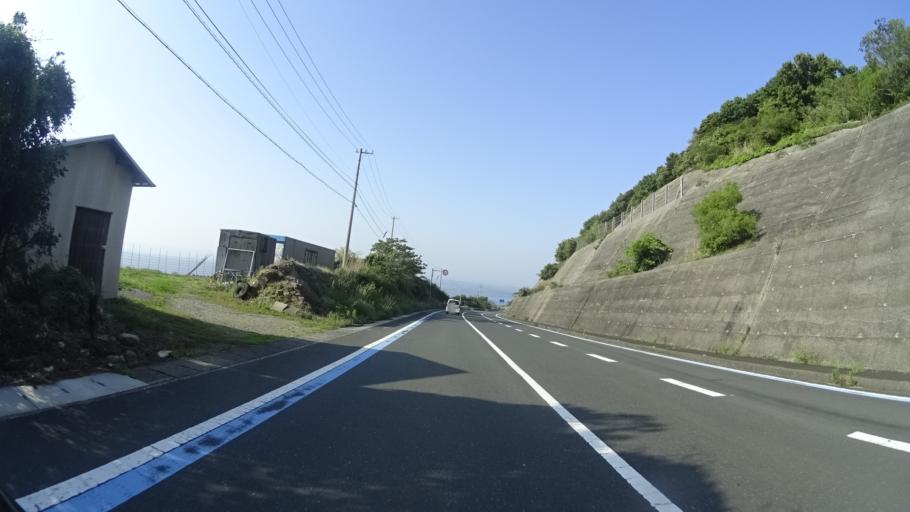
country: JP
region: Ehime
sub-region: Nishiuwa-gun
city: Ikata-cho
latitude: 33.4075
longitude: 132.1723
